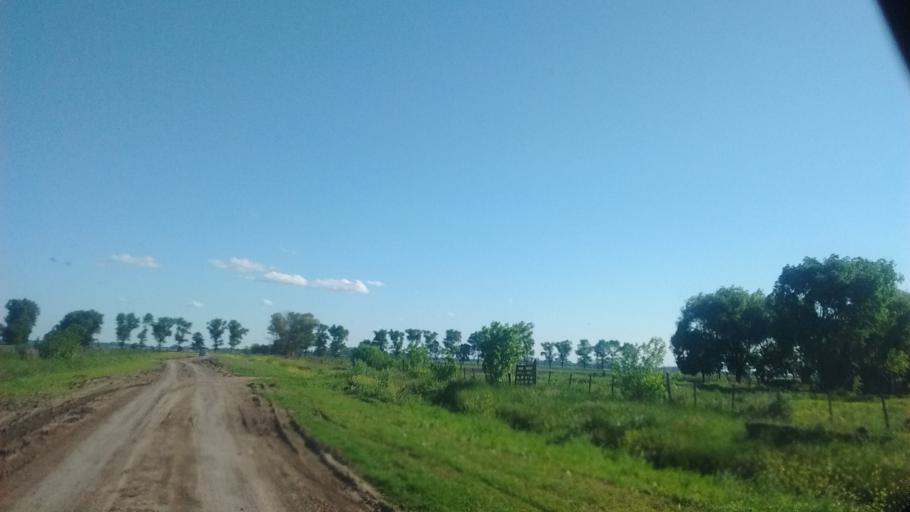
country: AR
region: Santa Fe
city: Funes
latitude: -32.8694
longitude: -60.7985
